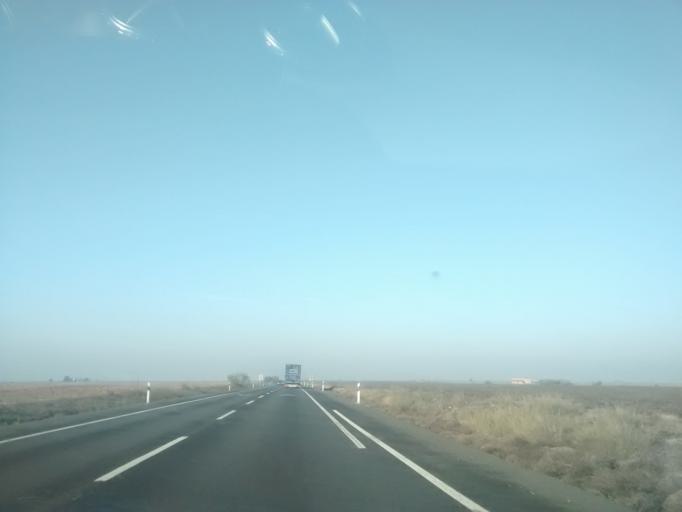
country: ES
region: Aragon
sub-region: Provincia de Huesca
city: Fraga
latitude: 41.5150
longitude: 0.2632
